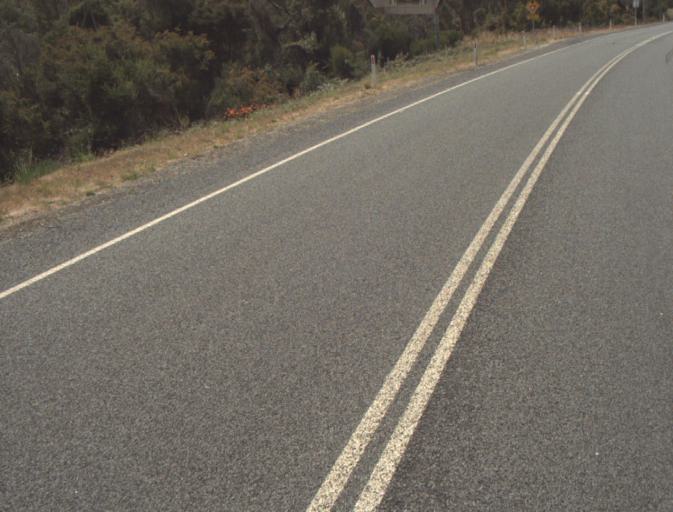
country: AU
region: Tasmania
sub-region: Launceston
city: Mayfield
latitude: -41.3038
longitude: 147.0488
